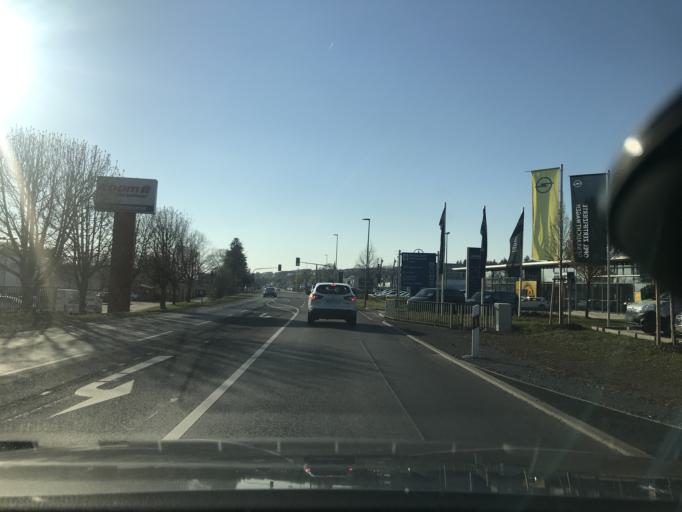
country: DE
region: Thuringia
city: Nordhausen
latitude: 51.4924
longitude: 10.8223
